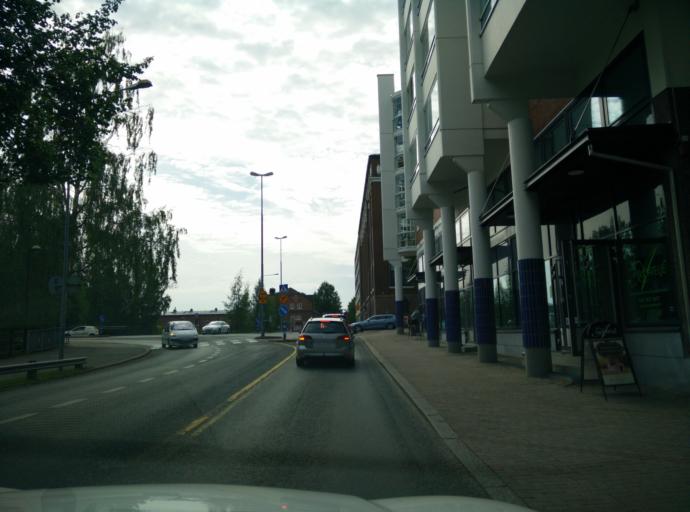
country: FI
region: Haeme
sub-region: Haemeenlinna
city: Haemeenlinna
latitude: 60.9978
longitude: 24.4707
